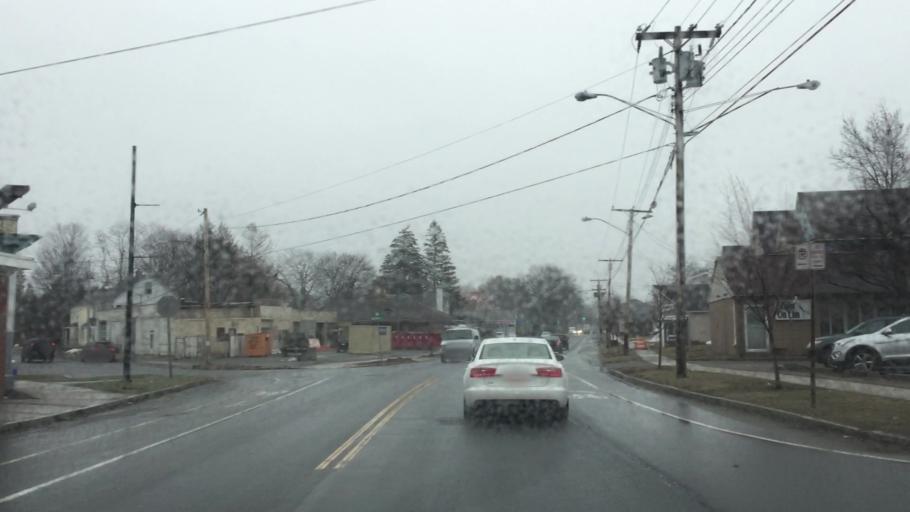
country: US
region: Massachusetts
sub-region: Berkshire County
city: Pittsfield
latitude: 42.4442
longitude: -73.2400
